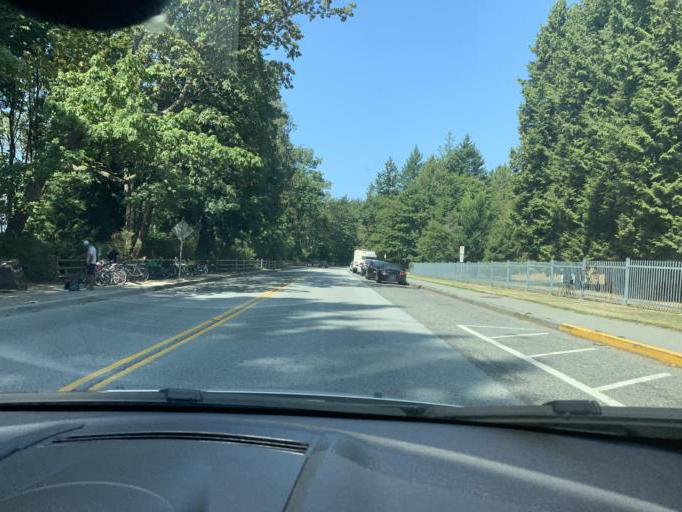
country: CA
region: British Columbia
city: West End
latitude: 49.2634
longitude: -123.2591
